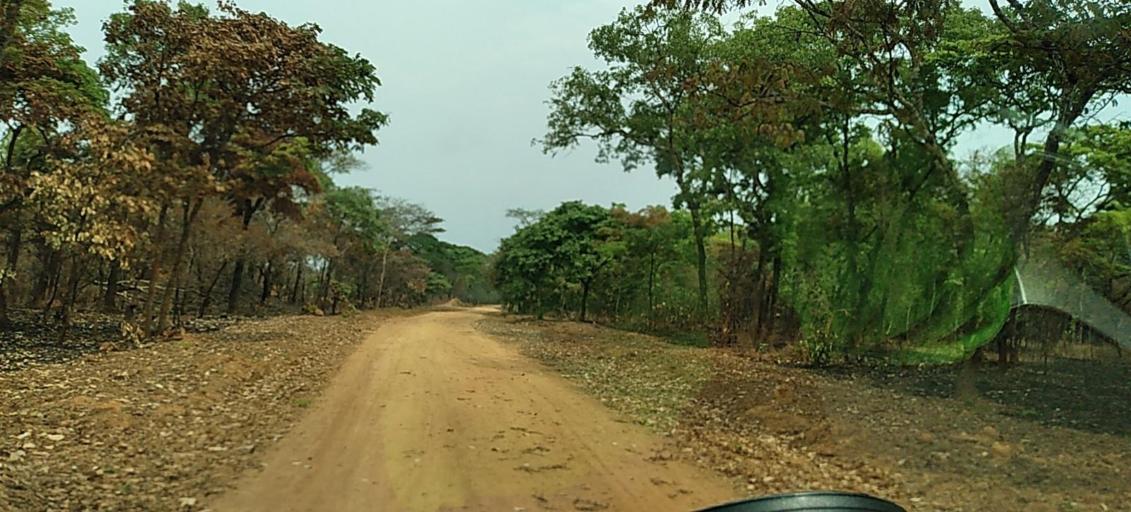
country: ZM
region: North-Western
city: Solwezi
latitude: -12.9581
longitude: 26.5665
